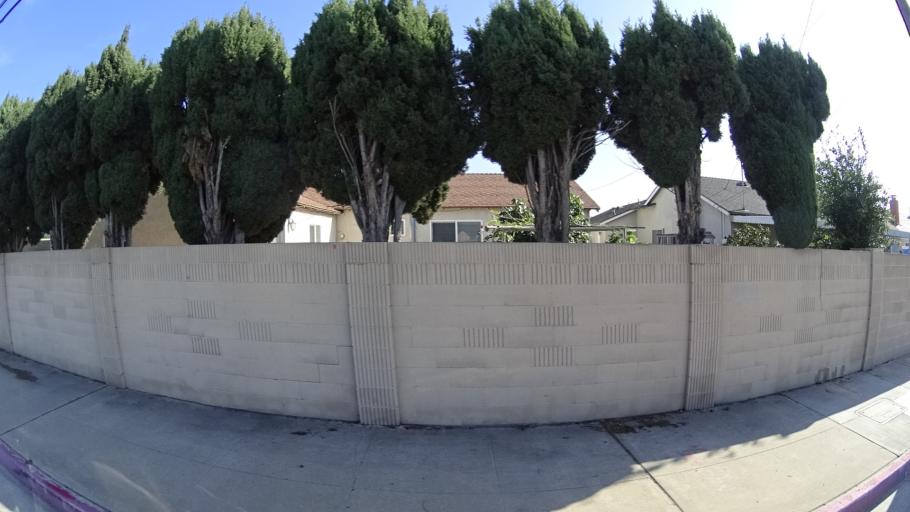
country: US
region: California
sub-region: Orange County
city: Midway City
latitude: 33.7415
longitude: -117.9807
